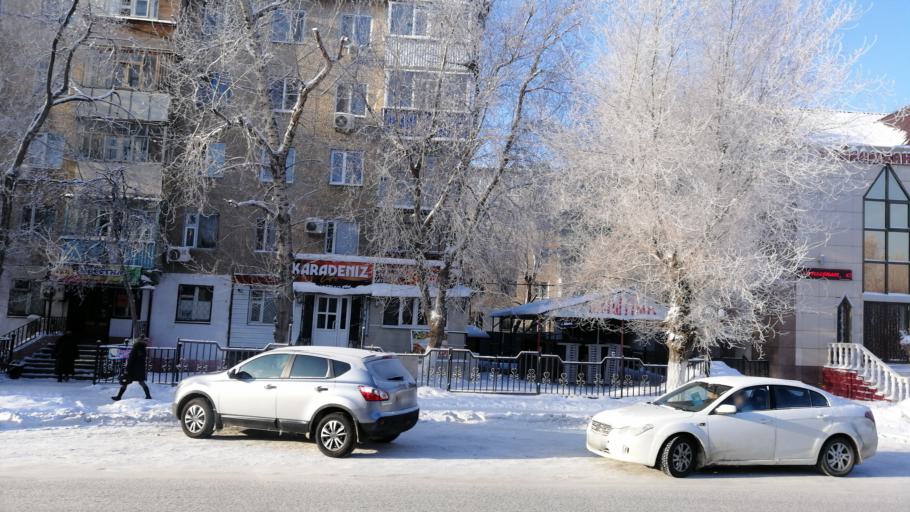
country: KZ
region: Aqtoebe
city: Aqtobe
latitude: 50.3063
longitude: 57.1503
